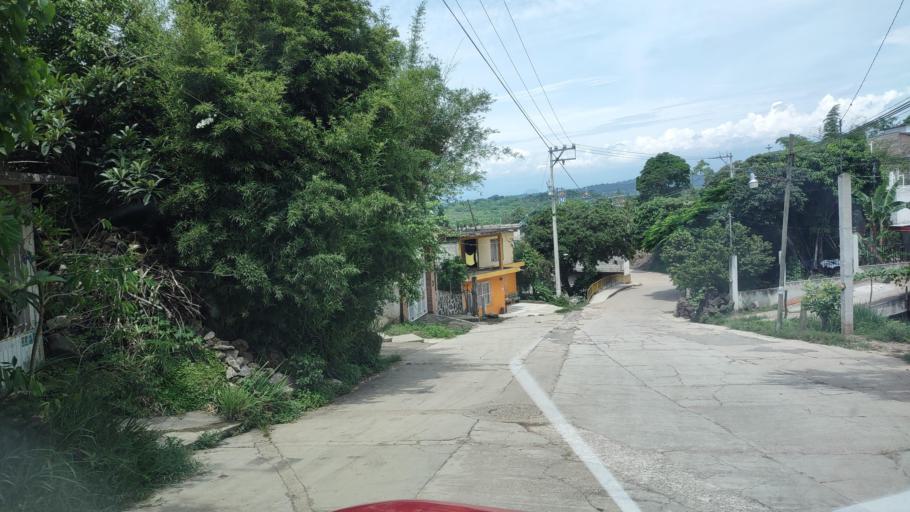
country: MX
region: Veracruz
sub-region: Emiliano Zapata
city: Jacarandas
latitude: 19.4663
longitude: -96.8343
